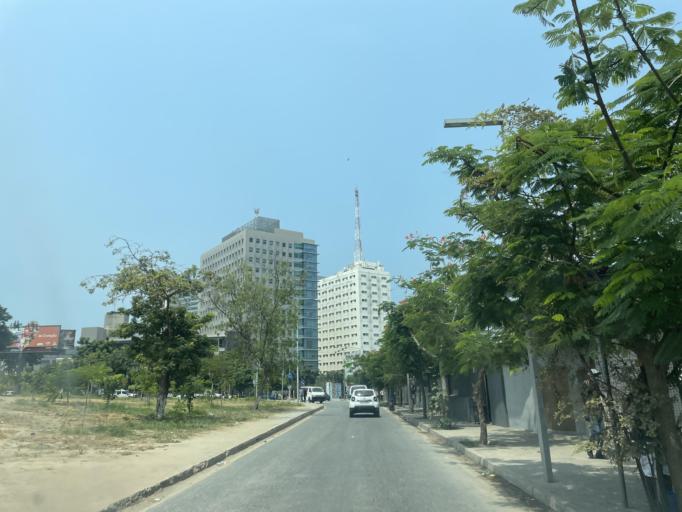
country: AO
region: Luanda
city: Luanda
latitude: -8.8095
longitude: 13.2419
